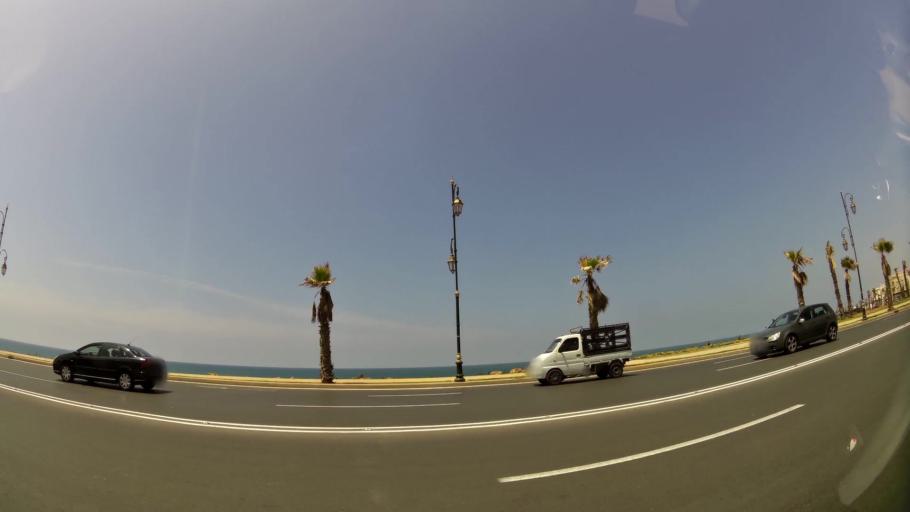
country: MA
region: Rabat-Sale-Zemmour-Zaer
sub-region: Rabat
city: Rabat
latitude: 34.0117
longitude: -6.8644
